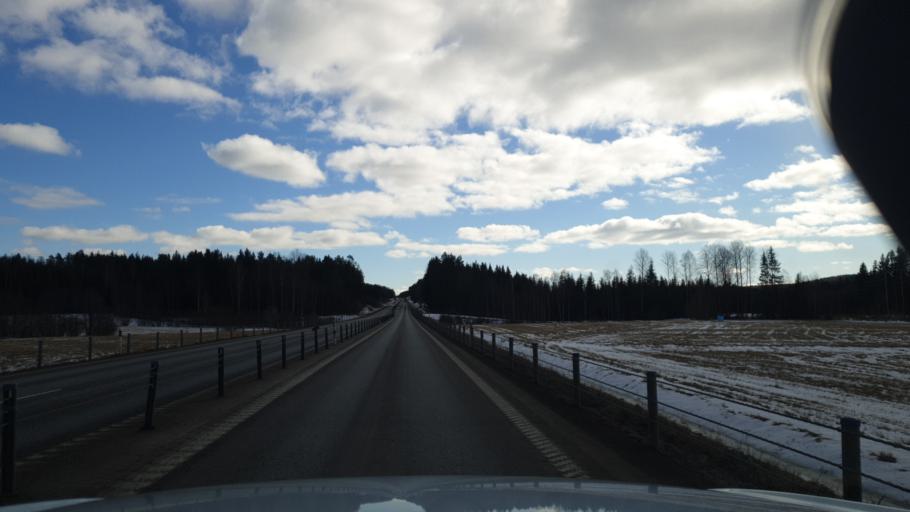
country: SE
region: Vaermland
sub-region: Arvika Kommun
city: Arvika
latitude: 59.6529
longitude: 12.6623
